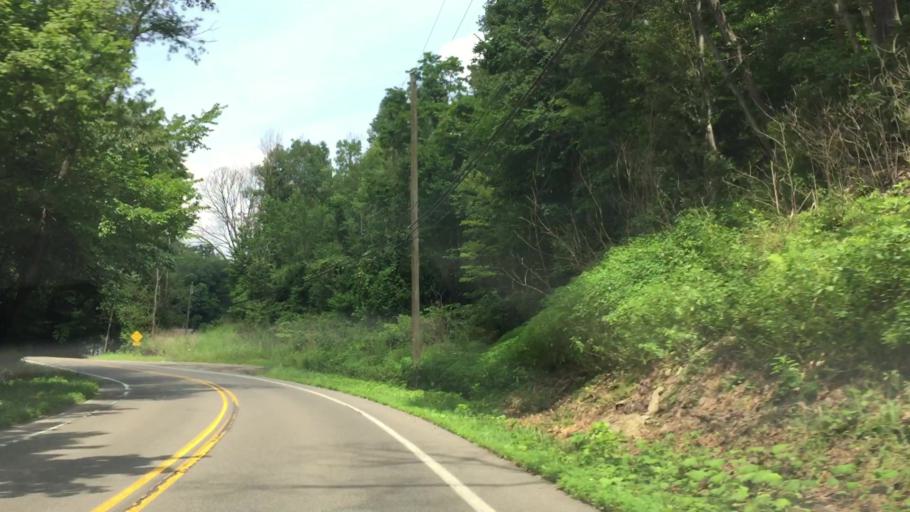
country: US
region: Pennsylvania
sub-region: Allegheny County
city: Enlow
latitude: 40.4487
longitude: -80.2095
